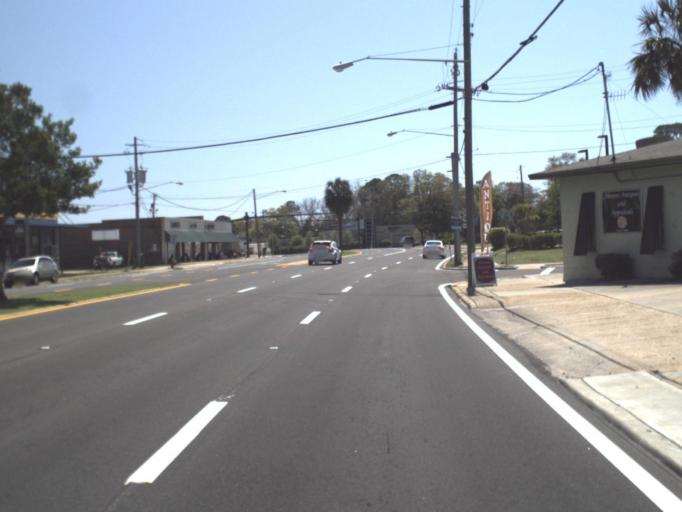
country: US
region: Florida
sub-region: Okaloosa County
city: Fort Walton Beach
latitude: 30.4066
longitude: -86.6051
